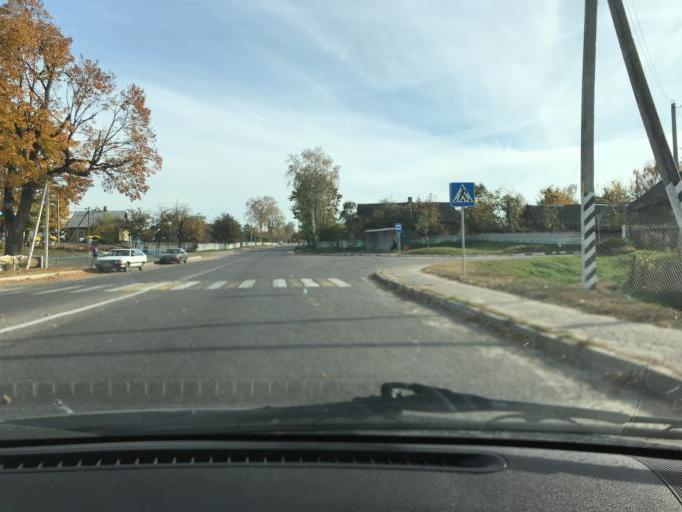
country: BY
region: Brest
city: Asnyezhytsy
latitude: 52.1968
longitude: 26.0683
